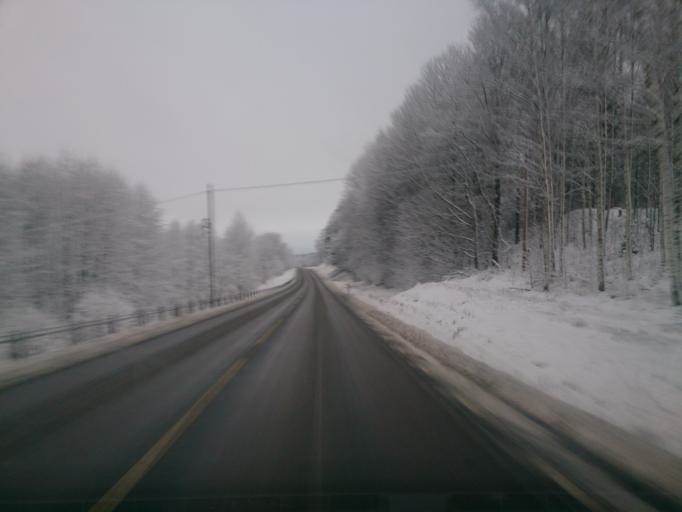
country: SE
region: OEstergoetland
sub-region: Atvidabergs Kommun
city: Atvidaberg
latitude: 58.2786
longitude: 15.9087
